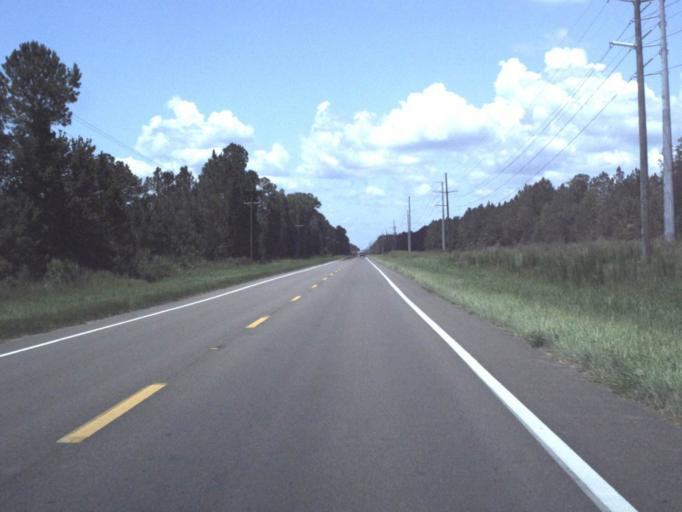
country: US
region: Florida
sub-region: Gilchrist County
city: Trenton
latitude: 29.6487
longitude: -82.7886
